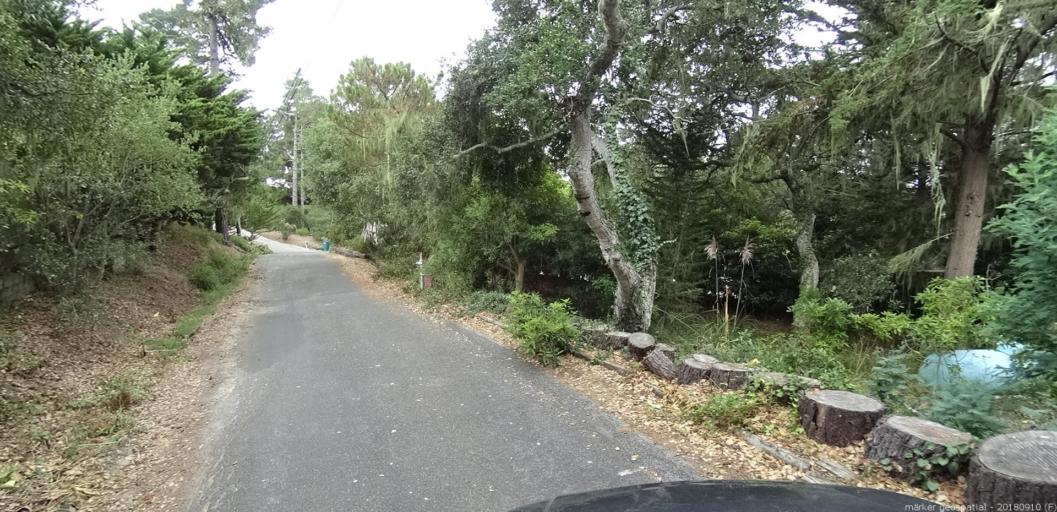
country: US
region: California
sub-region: Monterey County
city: Carmel-by-the-Sea
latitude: 36.4956
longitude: -121.9328
